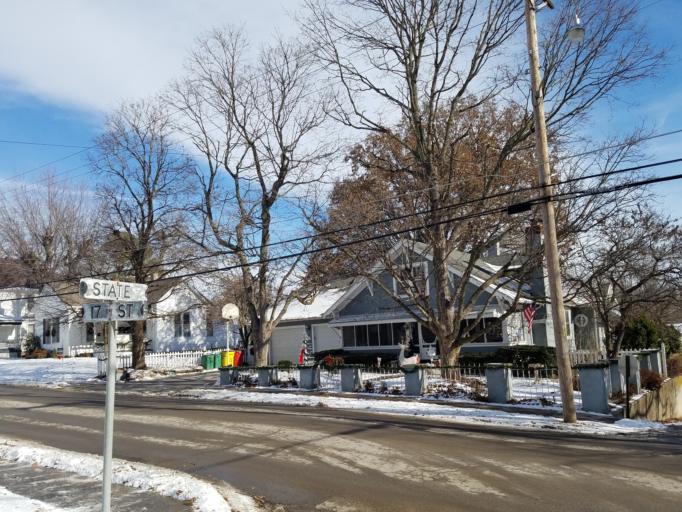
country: US
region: Missouri
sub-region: Lafayette County
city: Lexington
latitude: 39.1893
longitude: -93.8752
